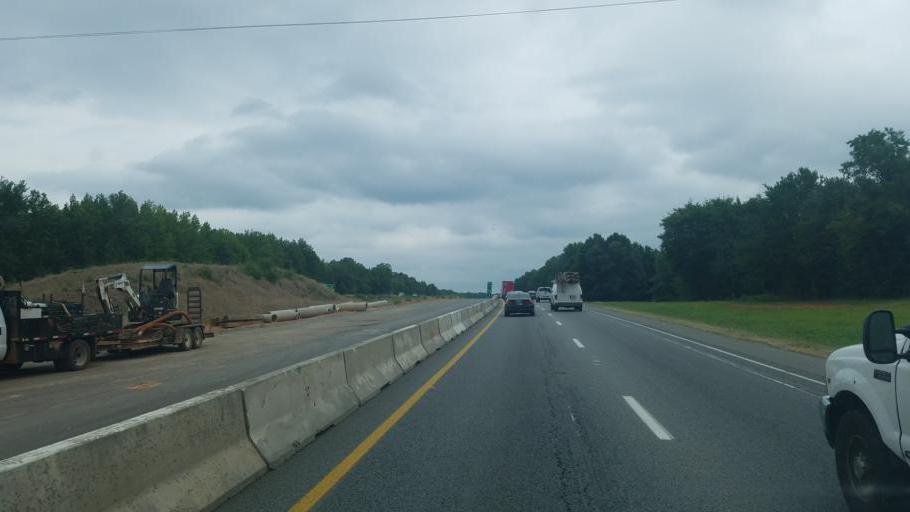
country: US
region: North Carolina
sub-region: Mecklenburg County
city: Cornelius
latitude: 35.4503
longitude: -80.8698
